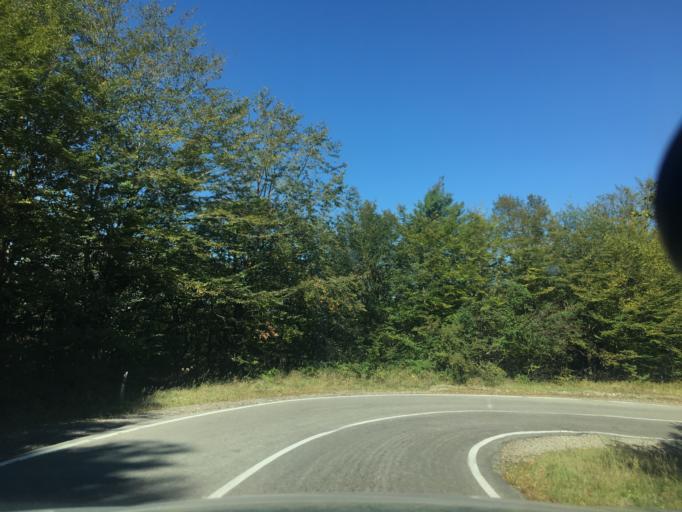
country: GE
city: Didi Lilo
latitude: 41.8768
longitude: 44.9094
